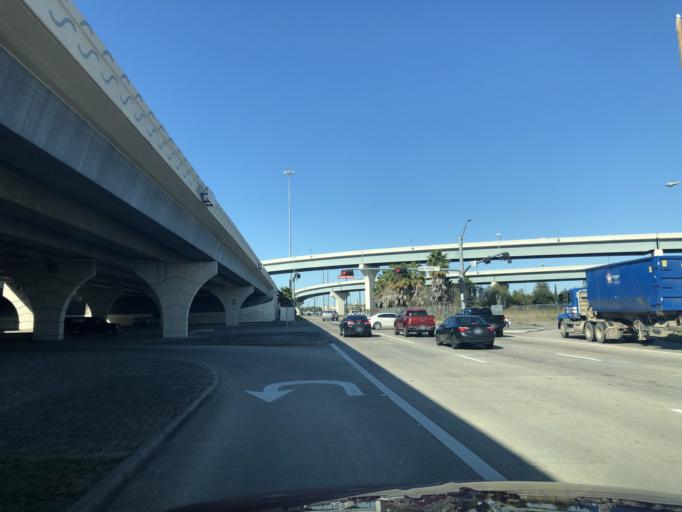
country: US
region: Texas
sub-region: Harris County
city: Webster
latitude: 29.5210
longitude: -95.1242
